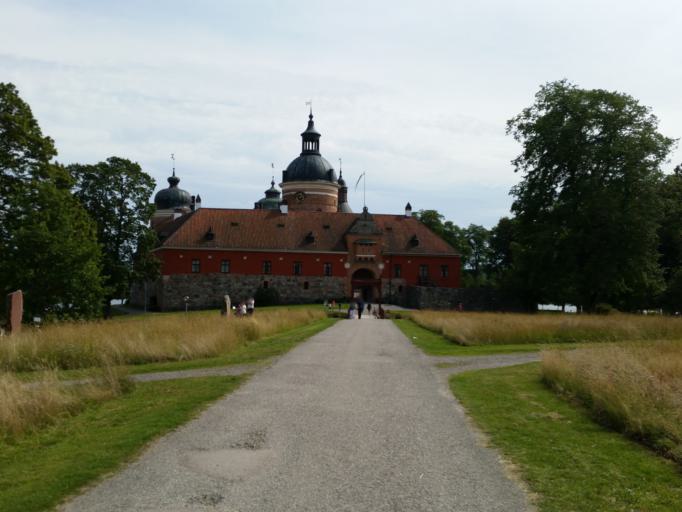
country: SE
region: Soedermanland
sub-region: Strangnas Kommun
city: Mariefred
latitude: 59.2573
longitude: 17.2175
